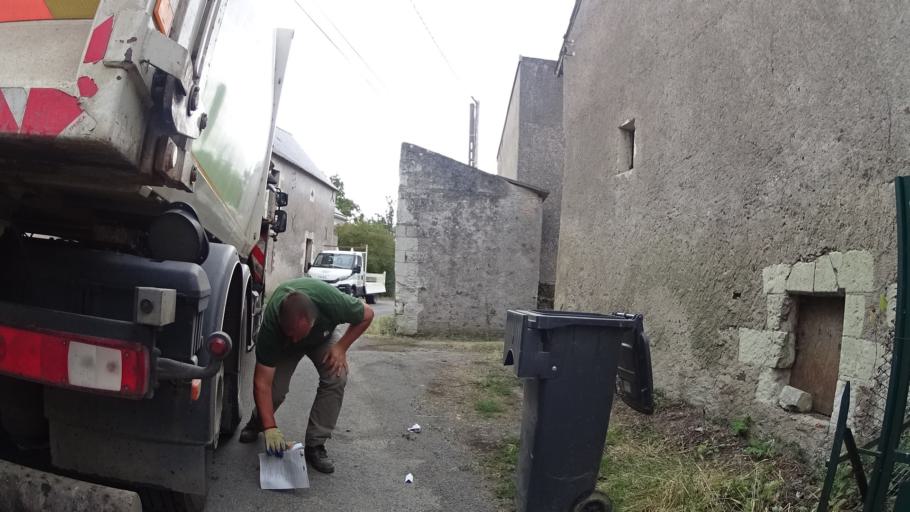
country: FR
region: Pays de la Loire
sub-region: Departement de Maine-et-Loire
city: Chalonnes-sur-Loire
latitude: 47.3676
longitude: -0.7686
